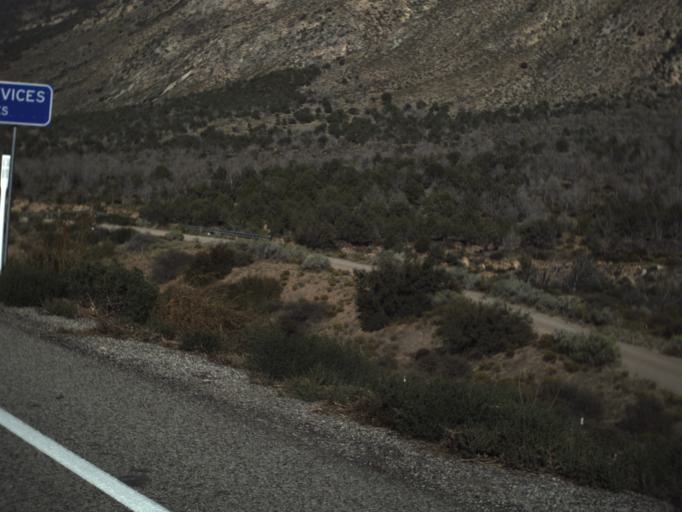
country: US
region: Utah
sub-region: Washington County
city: Toquerville
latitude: 37.3606
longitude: -113.2622
